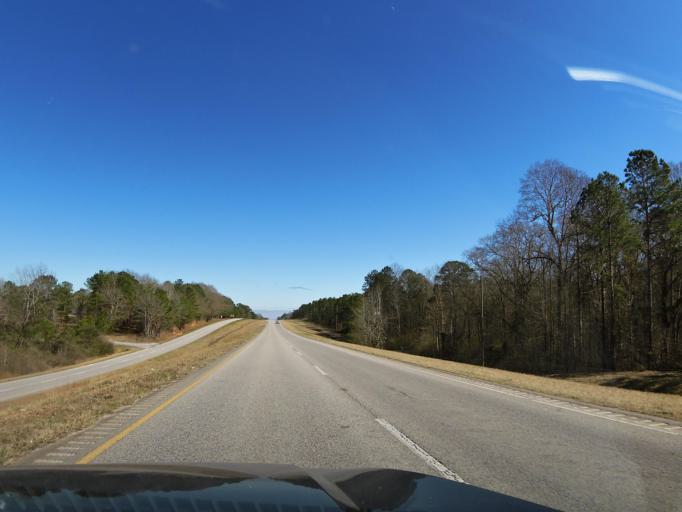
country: US
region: Alabama
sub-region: Bullock County
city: Union Springs
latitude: 32.1461
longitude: -85.6784
